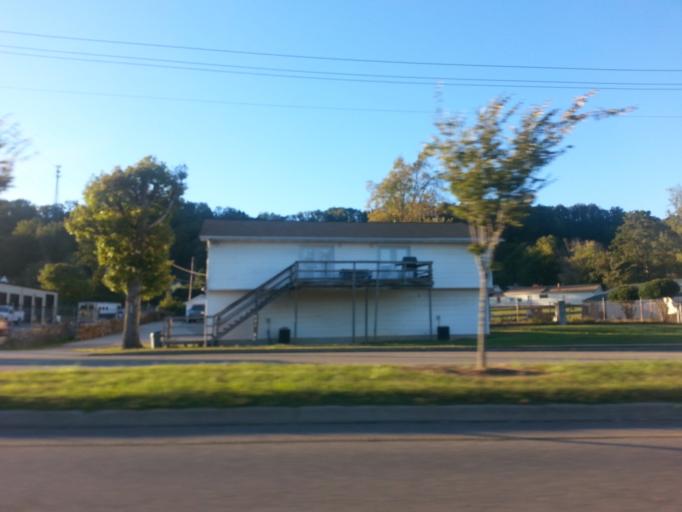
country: US
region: Tennessee
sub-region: Knox County
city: Knoxville
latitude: 36.0128
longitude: -84.0158
